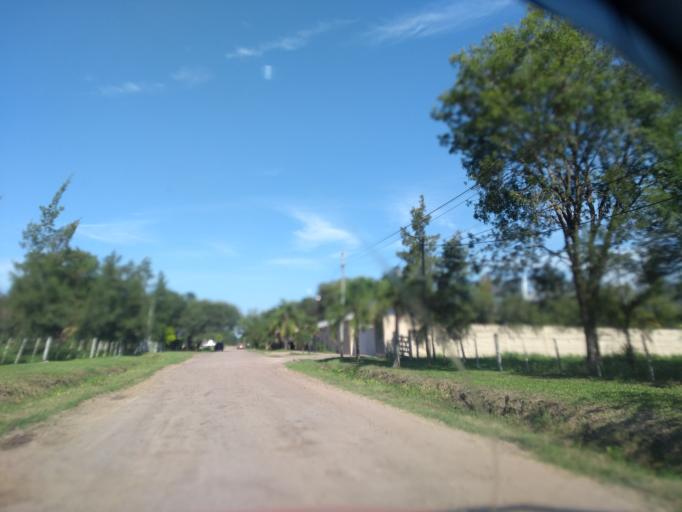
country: AR
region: Chaco
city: Resistencia
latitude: -27.4291
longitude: -58.9414
